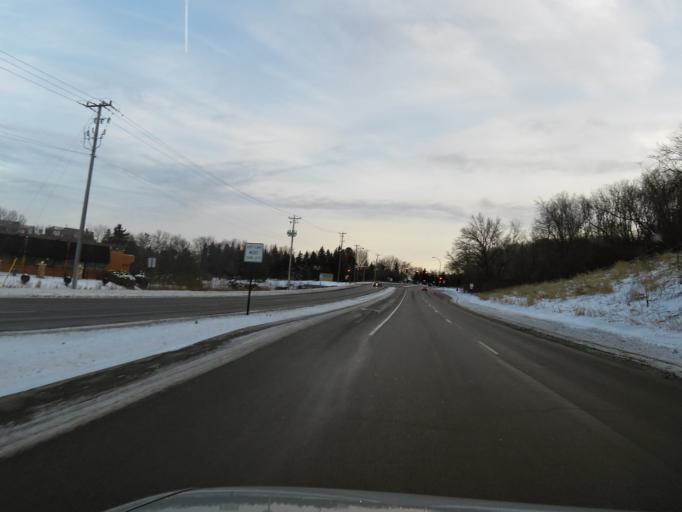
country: US
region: Minnesota
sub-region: Hennepin County
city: Minnetonka Mills
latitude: 44.8995
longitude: -93.4235
